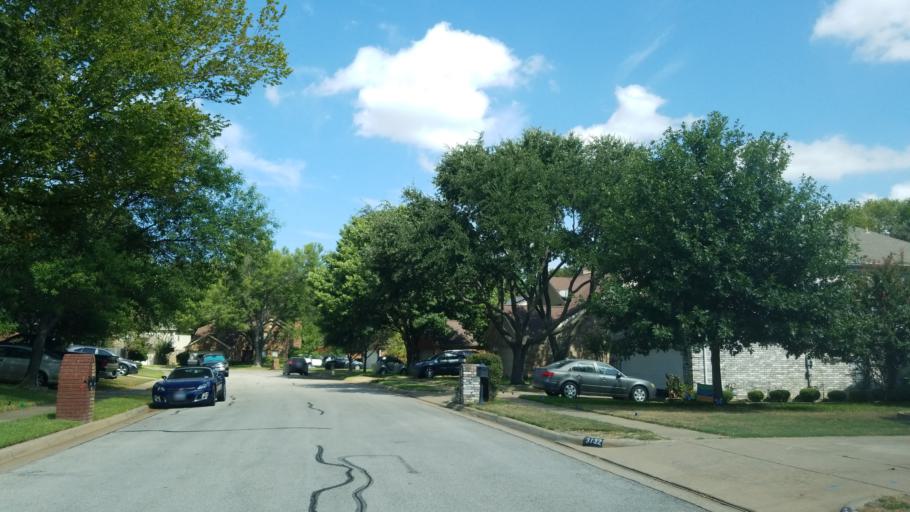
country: US
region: Texas
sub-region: Tarrant County
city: Euless
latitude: 32.8540
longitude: -97.1025
